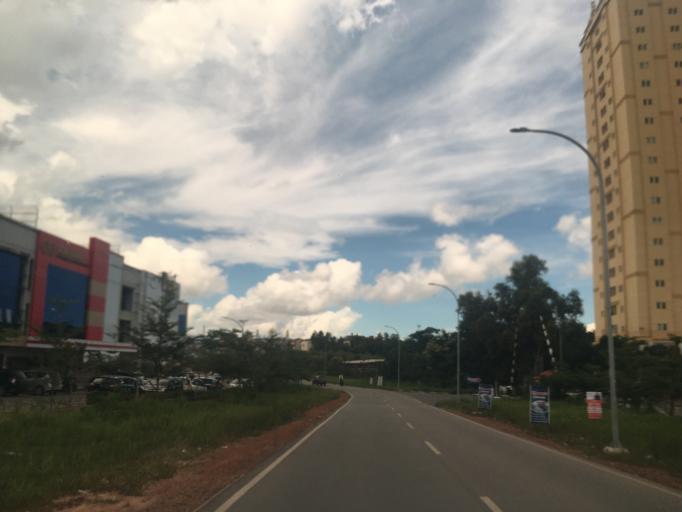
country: SG
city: Singapore
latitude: 1.1185
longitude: 104.0267
